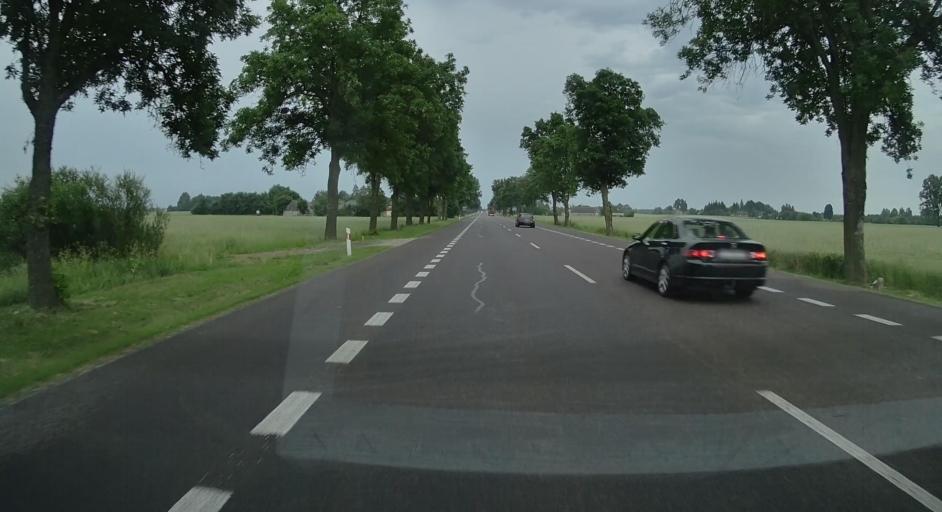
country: PL
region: Lublin Voivodeship
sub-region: Powiat bialski
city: Rzeczyca
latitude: 52.0397
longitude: 22.6902
